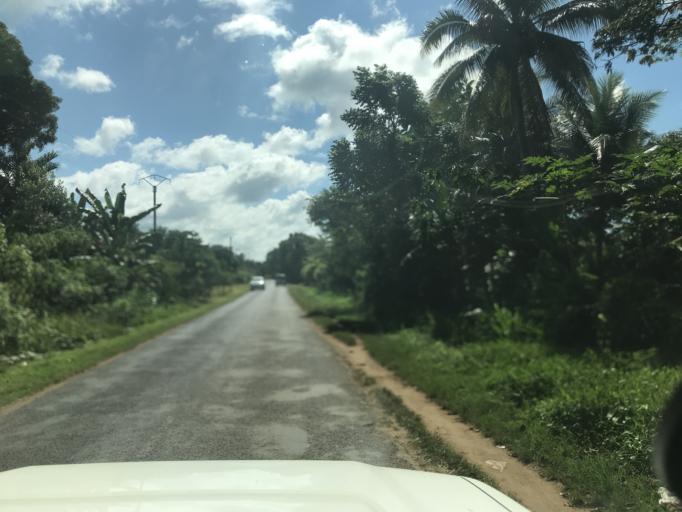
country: VU
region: Sanma
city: Luganville
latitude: -15.5303
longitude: 167.1545
